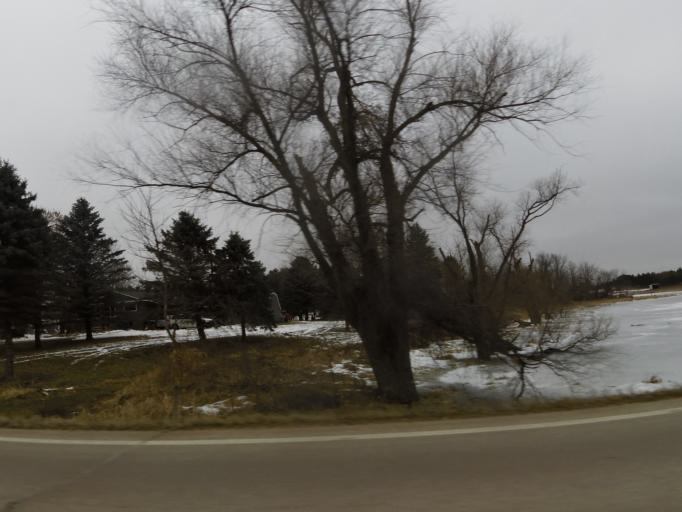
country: US
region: Minnesota
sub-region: Carver County
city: Carver
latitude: 44.7179
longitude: -93.6748
